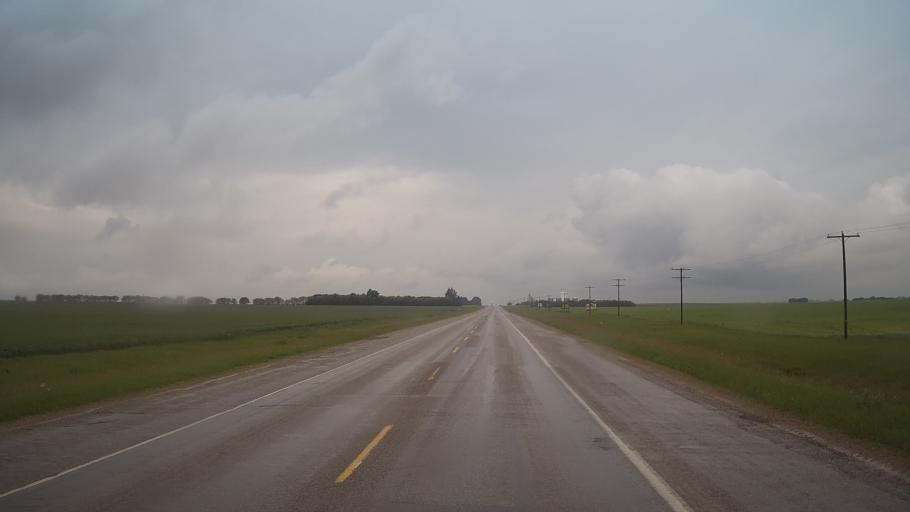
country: CA
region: Saskatchewan
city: Unity
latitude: 52.4350
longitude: -109.0742
